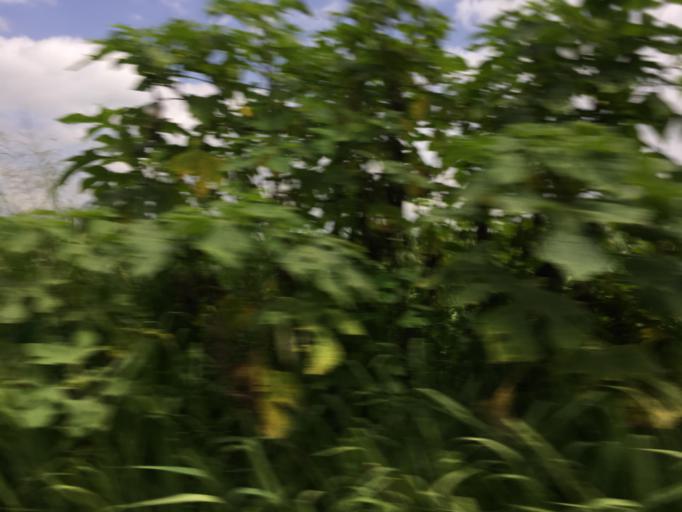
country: GT
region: Guatemala
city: Villa Canales
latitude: 14.4503
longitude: -90.5262
